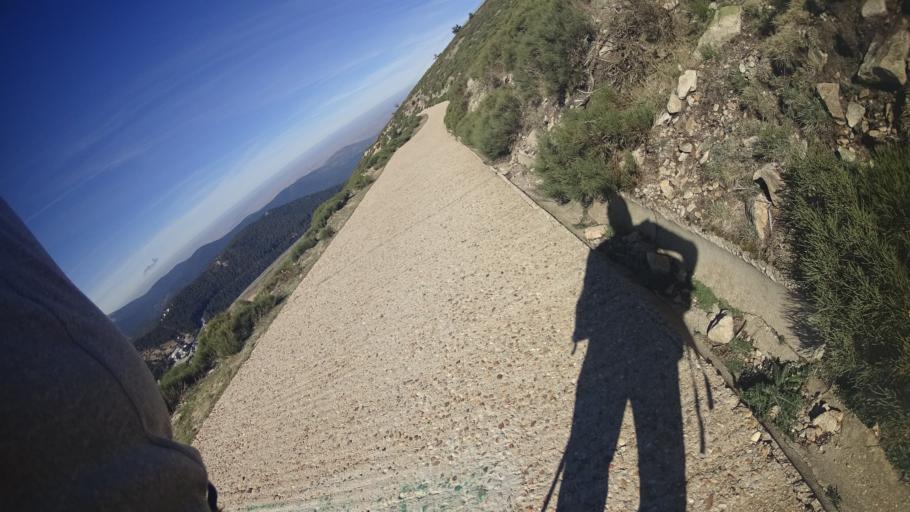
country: ES
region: Madrid
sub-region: Provincia de Madrid
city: Navacerrada
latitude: 40.7836
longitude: -3.9939
